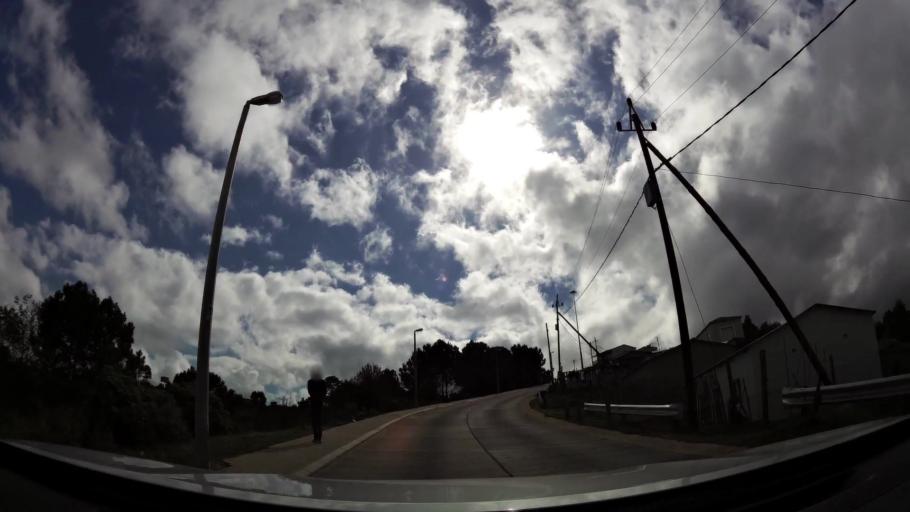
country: ZA
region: Western Cape
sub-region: Eden District Municipality
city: Knysna
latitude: -34.0312
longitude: 23.0999
